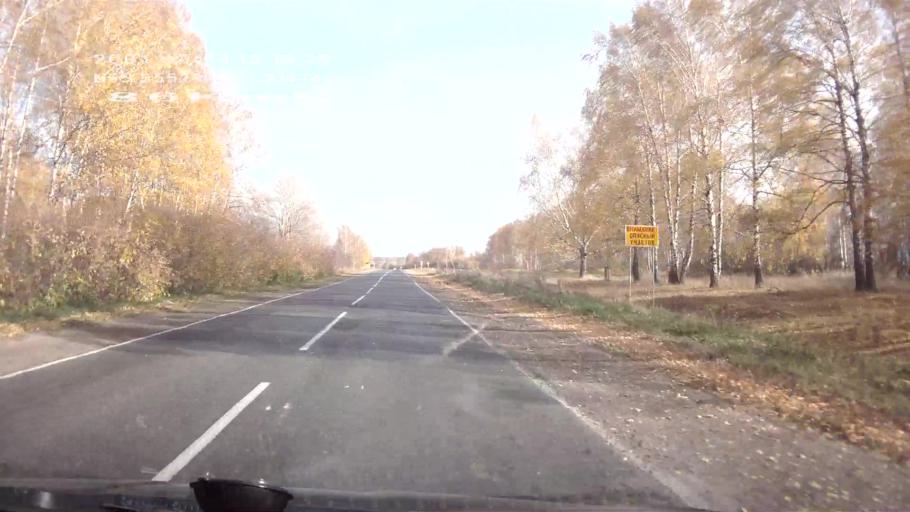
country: RU
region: Chuvashia
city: Ibresi
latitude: 55.3553
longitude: 47.2143
